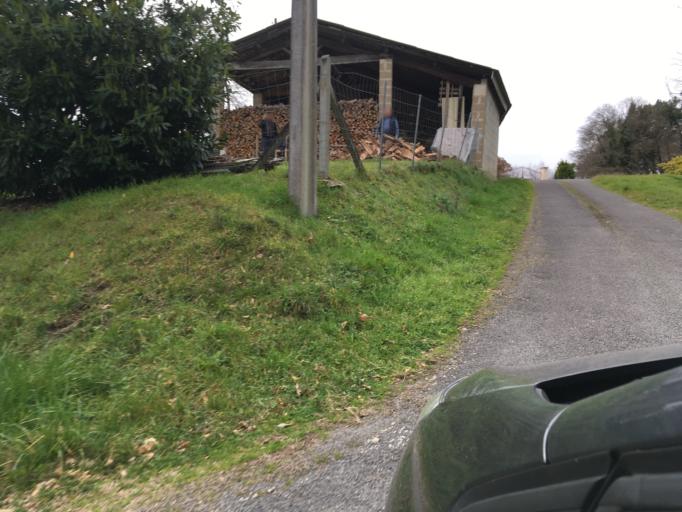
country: FR
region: Aquitaine
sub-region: Departement de la Gironde
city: Saint-Ciers-sur-Gironde
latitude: 45.3191
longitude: -0.5946
